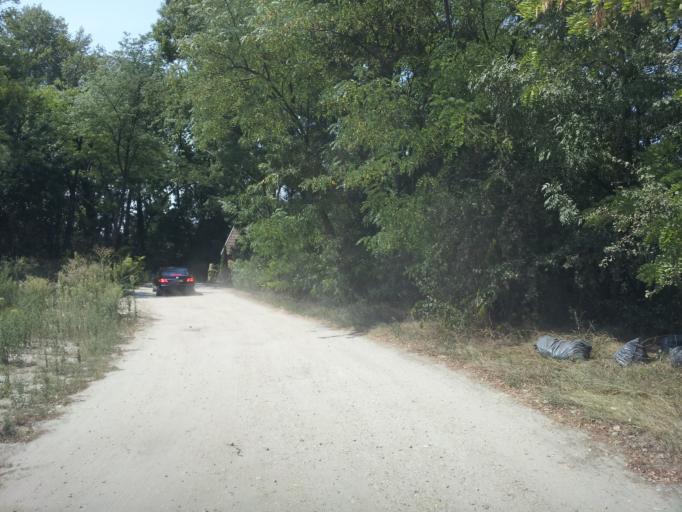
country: HU
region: Pest
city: Szigethalom
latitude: 47.3068
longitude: 19.0348
